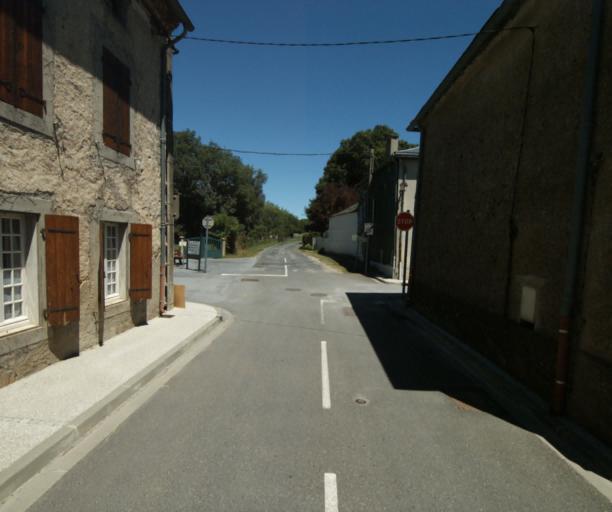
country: FR
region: Midi-Pyrenees
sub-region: Departement du Tarn
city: Dourgne
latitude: 43.4313
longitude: 2.1705
